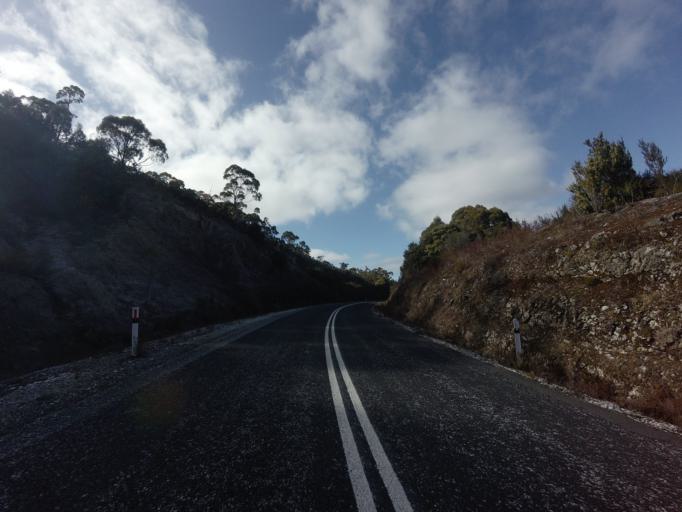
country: AU
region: Tasmania
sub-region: West Coast
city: Queenstown
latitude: -42.7949
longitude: 146.0860
